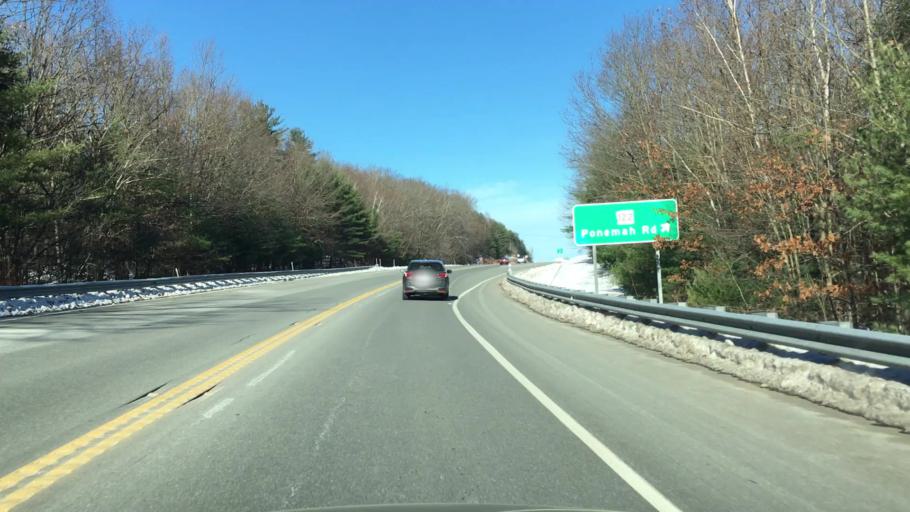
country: US
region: New Hampshire
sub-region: Hillsborough County
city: Milford
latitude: 42.8400
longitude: -71.6189
